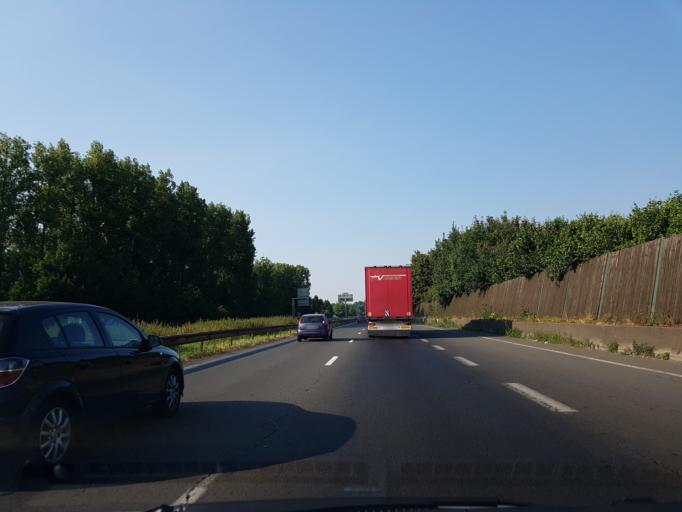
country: FR
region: Nord-Pas-de-Calais
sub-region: Departement du Nord
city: Neuville-en-Ferrain
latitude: 50.7528
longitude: 3.1471
